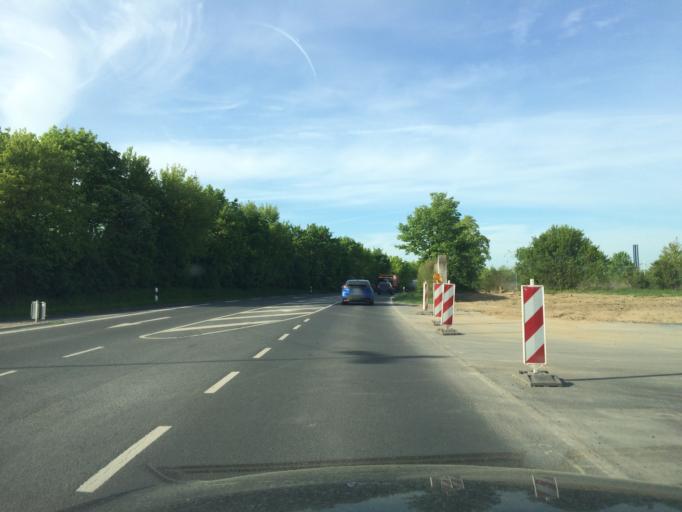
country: DE
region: Bavaria
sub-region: Regierungsbezirk Unterfranken
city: Gerbrunn
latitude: 49.7852
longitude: 9.9826
